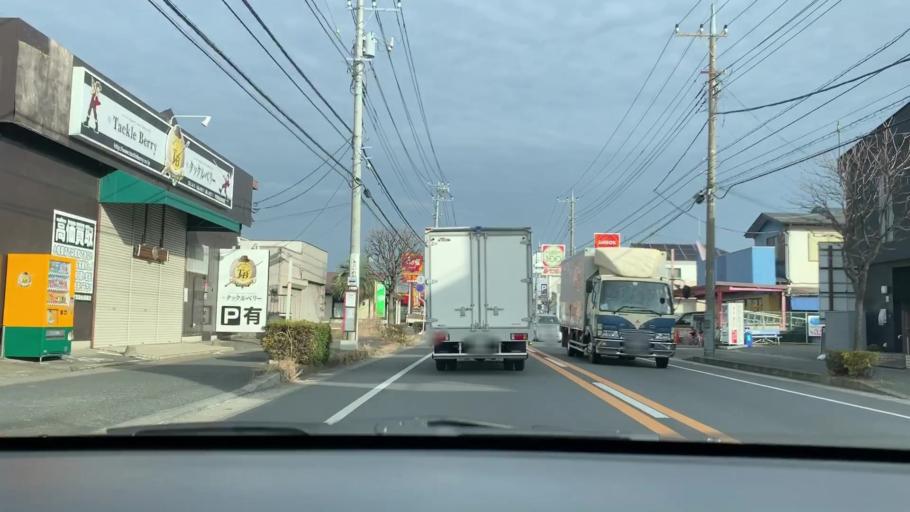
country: JP
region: Chiba
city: Nagareyama
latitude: 35.8407
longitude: 139.8971
